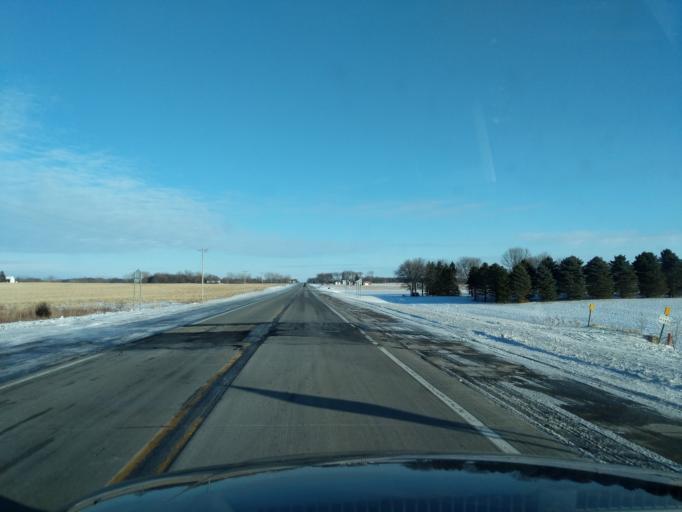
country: US
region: Minnesota
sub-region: McLeod County
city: Hutchinson
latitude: 44.8930
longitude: -94.3143
